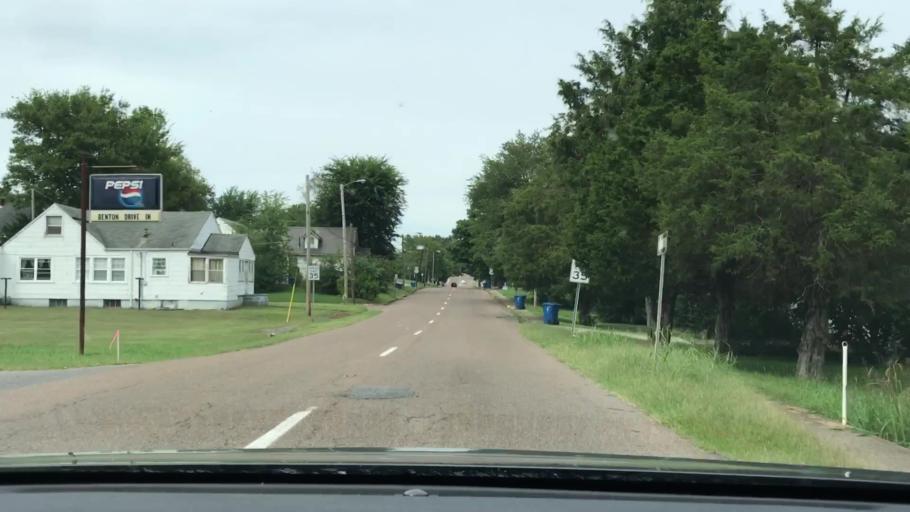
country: US
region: Kentucky
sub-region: Marshall County
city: Benton
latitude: 36.8525
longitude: -88.3499
